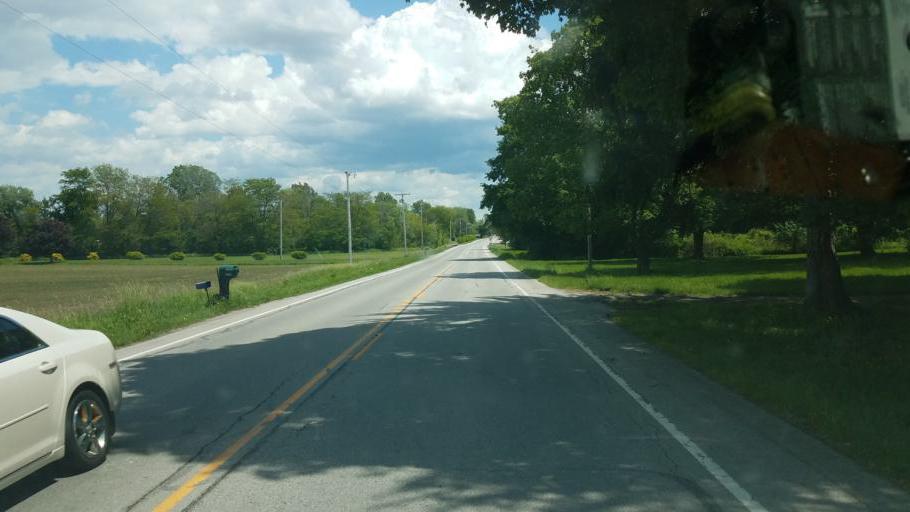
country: US
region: Ohio
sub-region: Crawford County
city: Crestline
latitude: 40.7944
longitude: -82.7555
